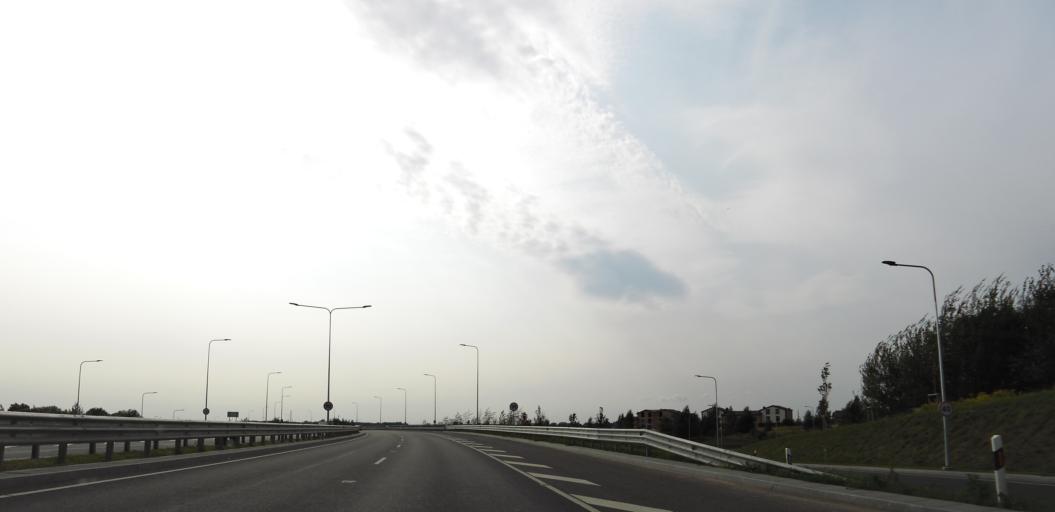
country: LT
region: Vilnius County
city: Pasilaiciai
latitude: 54.7375
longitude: 25.2100
